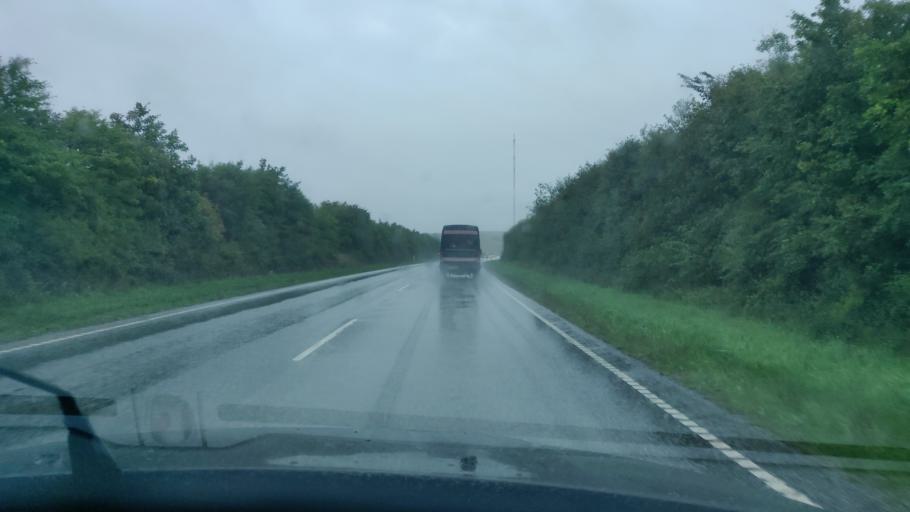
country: DK
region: North Denmark
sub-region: Thisted Kommune
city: Thisted
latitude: 56.9725
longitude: 8.6654
